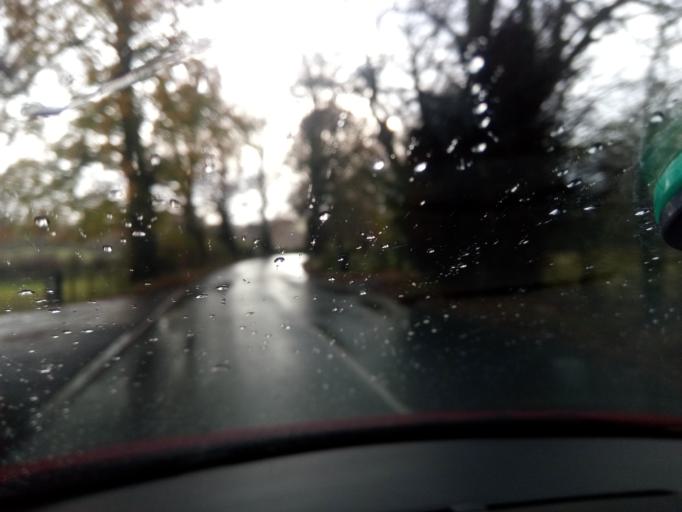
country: GB
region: England
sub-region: Northumberland
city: Birtley
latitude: 55.0975
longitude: -2.2238
